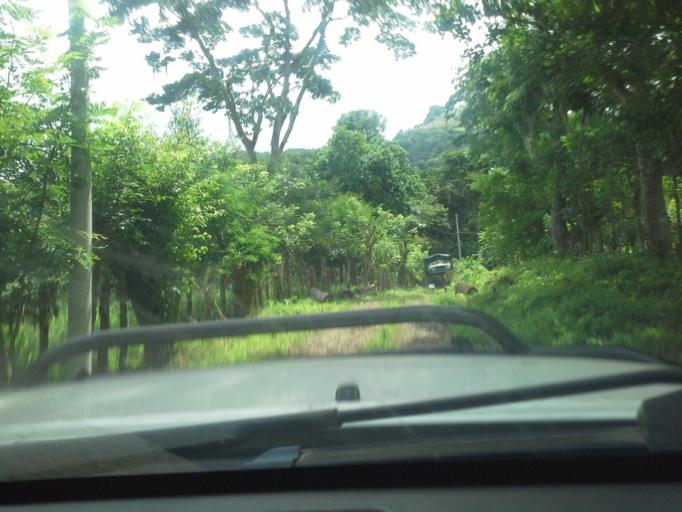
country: NI
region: Boaco
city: San Jose de los Remates
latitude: 12.6946
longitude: -85.7447
